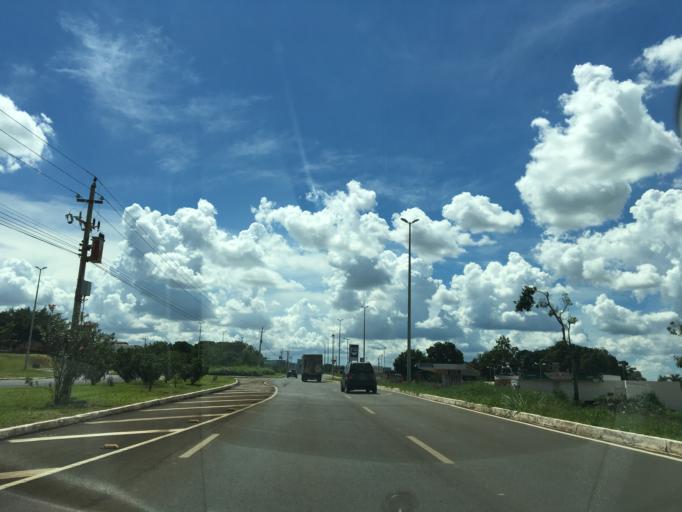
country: BR
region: Federal District
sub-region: Brasilia
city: Brasilia
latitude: -15.7898
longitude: -47.8483
